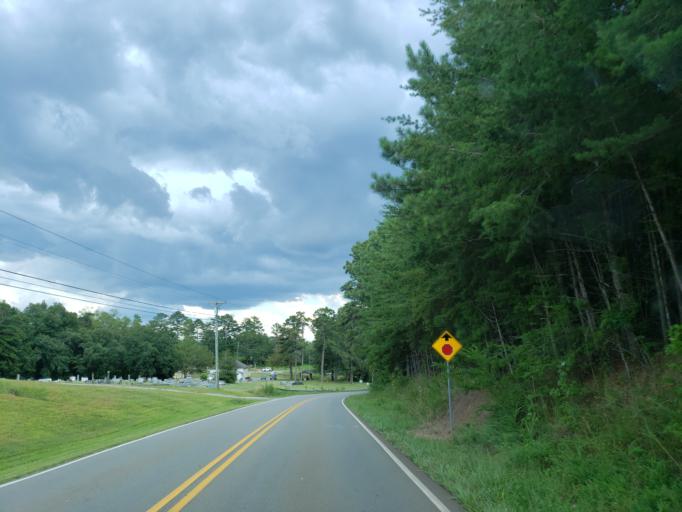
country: US
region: Georgia
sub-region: Pickens County
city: Jasper
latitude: 34.3940
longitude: -84.4680
